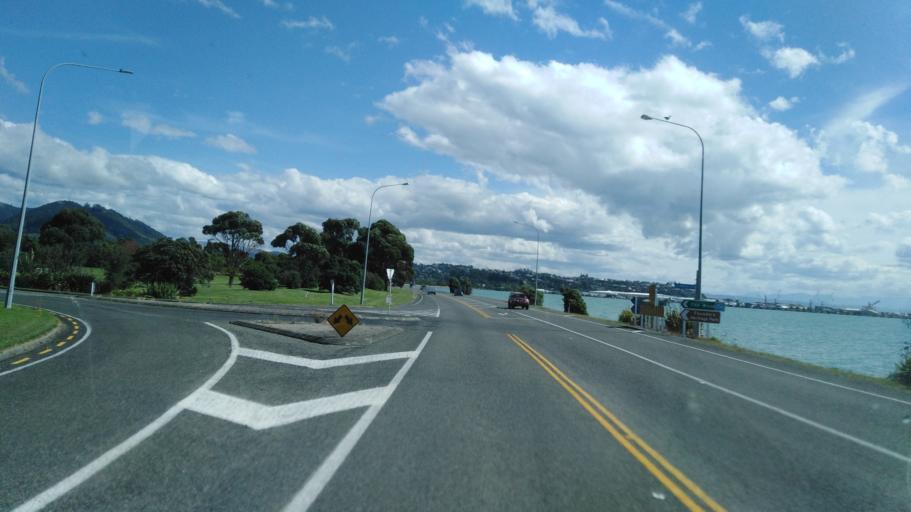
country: NZ
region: Nelson
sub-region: Nelson City
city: Nelson
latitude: -41.2559
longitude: 173.2993
